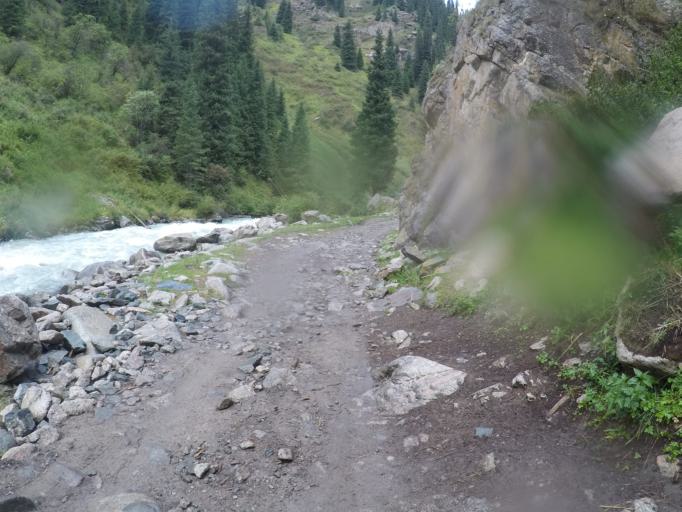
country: KG
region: Ysyk-Koel
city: Teploklyuchenka
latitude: 42.4146
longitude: 78.5717
